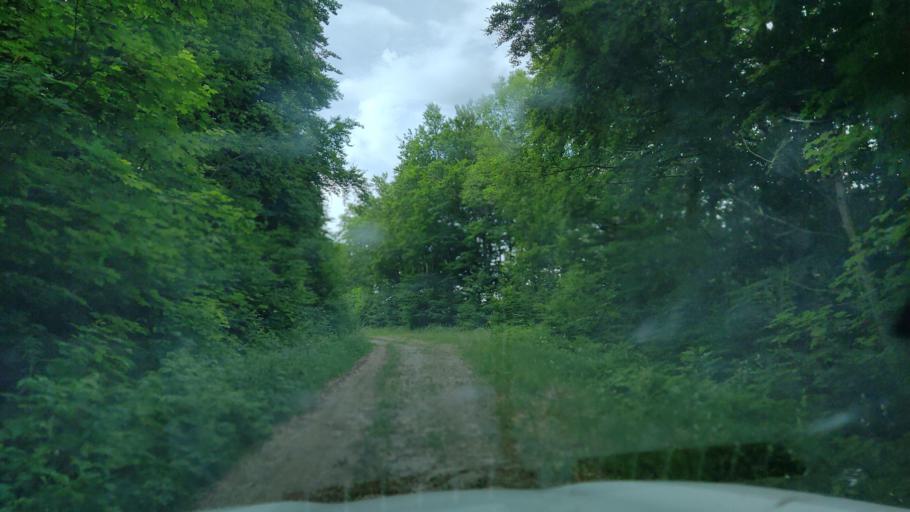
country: FR
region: Rhone-Alpes
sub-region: Departement de la Savoie
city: Cruet
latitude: 45.5959
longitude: 6.1062
